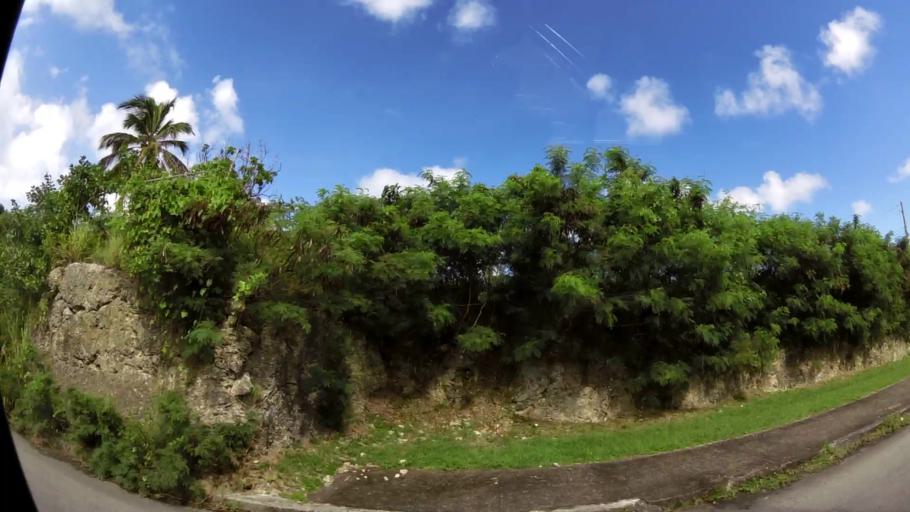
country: BB
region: Saint Lucy
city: Checker Hall
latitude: 13.2709
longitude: -59.6438
